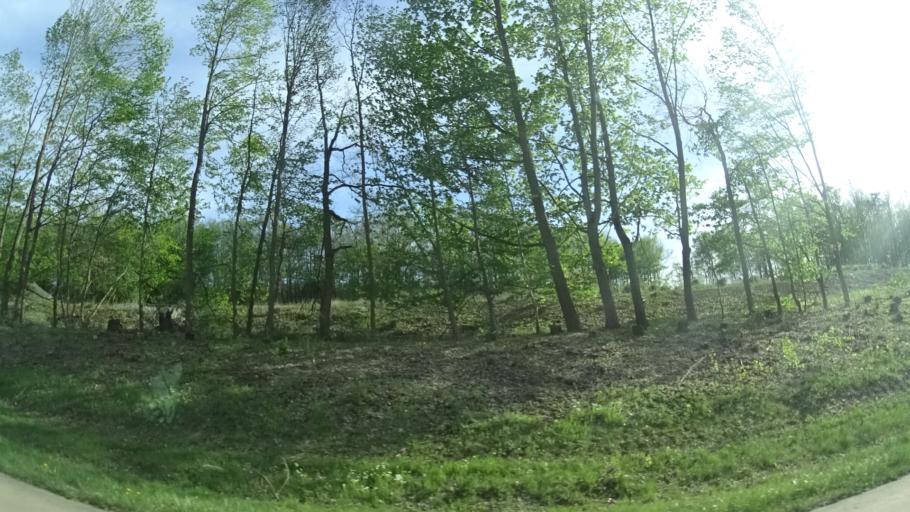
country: DE
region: Bavaria
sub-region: Regierungsbezirk Unterfranken
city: Grosslangheim
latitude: 49.7828
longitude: 10.2140
